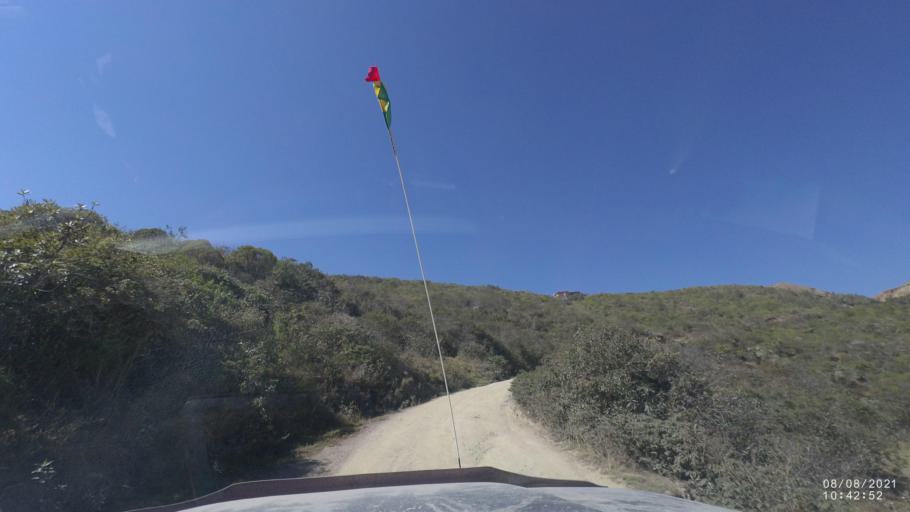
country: BO
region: La Paz
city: Quime
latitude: -16.7020
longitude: -66.7213
